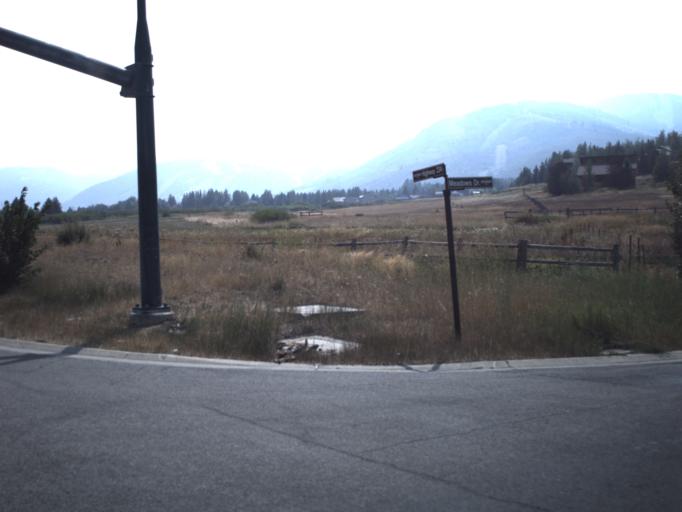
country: US
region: Utah
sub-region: Summit County
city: Snyderville
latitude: 40.6753
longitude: -111.5204
